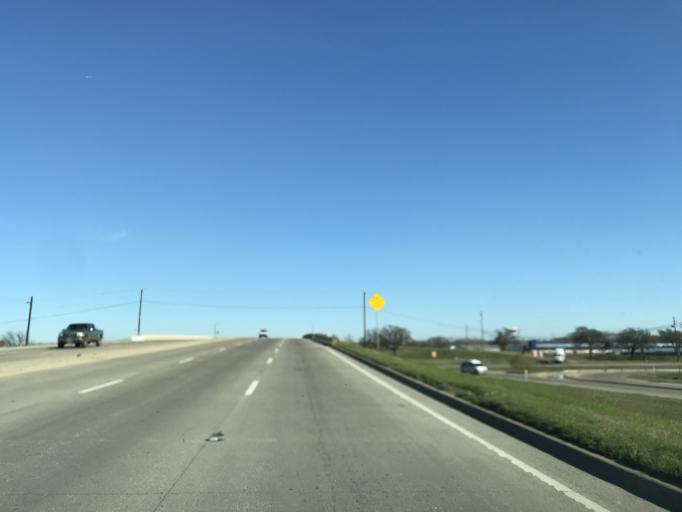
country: US
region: Texas
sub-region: Dallas County
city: Hutchins
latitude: 32.7025
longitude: -96.7487
